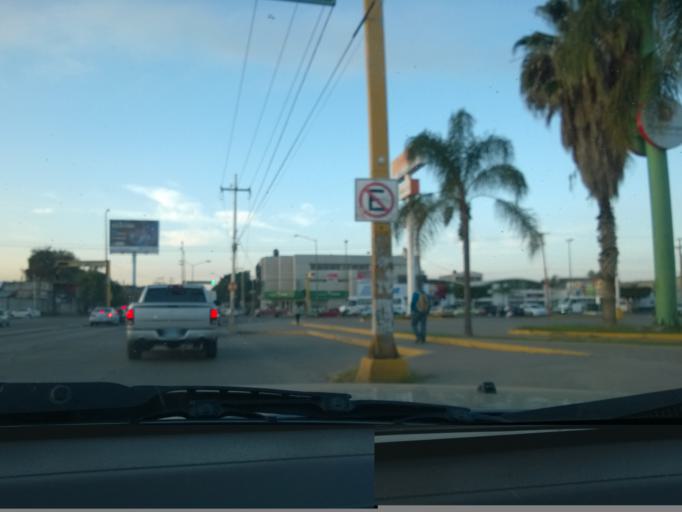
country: MX
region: Guanajuato
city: Leon
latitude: 21.1316
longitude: -101.6598
